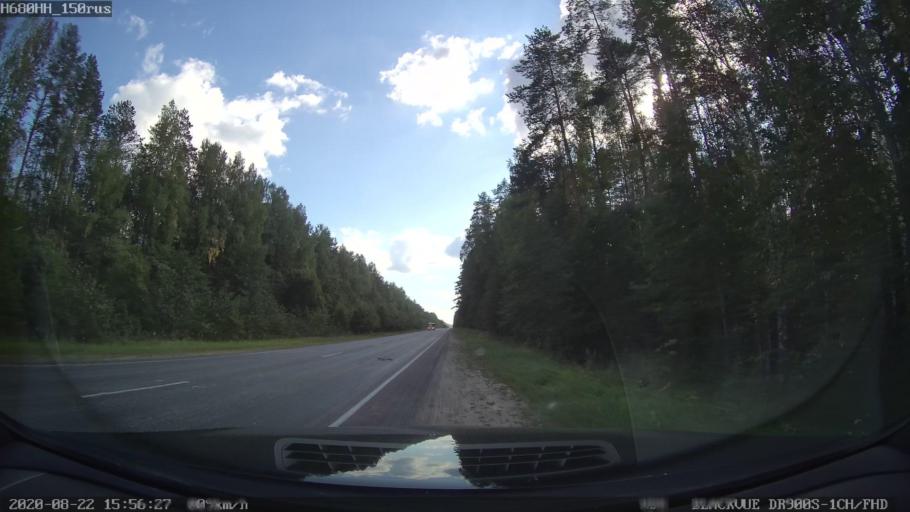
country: RU
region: Tverskaya
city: Bezhetsk
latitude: 57.6108
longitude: 36.3639
